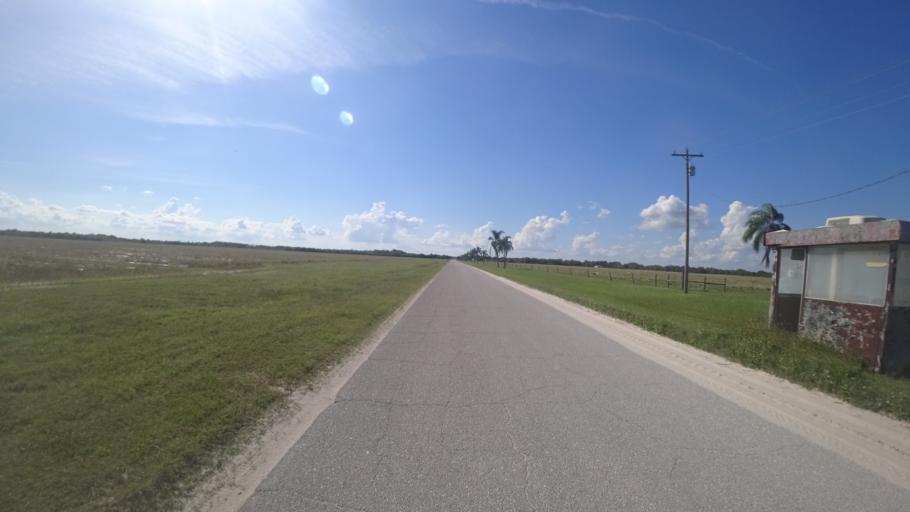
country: US
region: Florida
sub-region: Sarasota County
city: The Meadows
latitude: 27.4448
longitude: -82.2644
